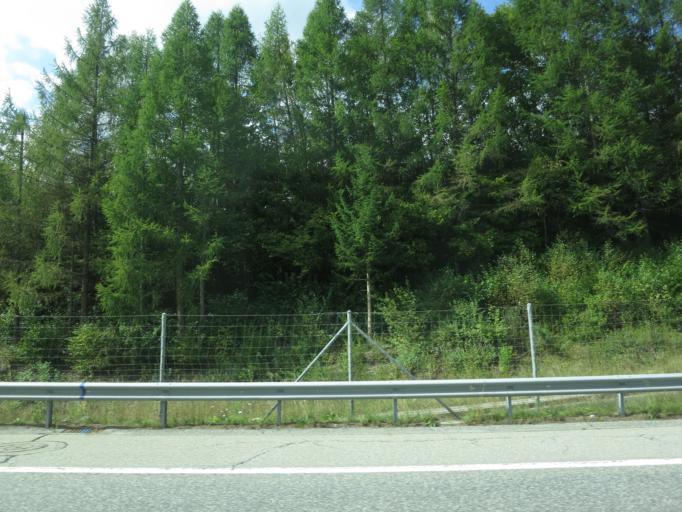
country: CH
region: Grisons
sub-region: Hinterrhein District
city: Thusis
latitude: 46.6340
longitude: 9.4382
